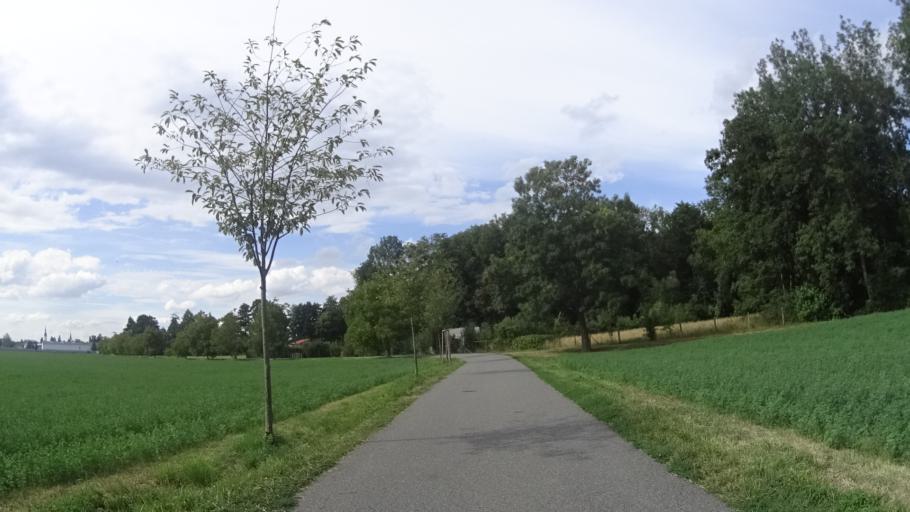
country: CZ
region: Olomoucky
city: Litovel
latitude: 49.6968
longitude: 17.0928
